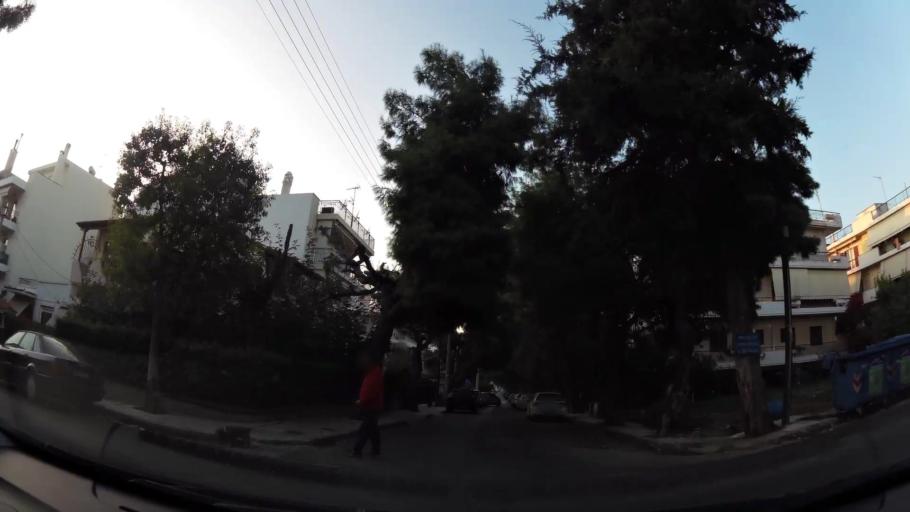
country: GR
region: Attica
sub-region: Nomarchia Athinas
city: Glyfada
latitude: 37.8859
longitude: 23.7641
